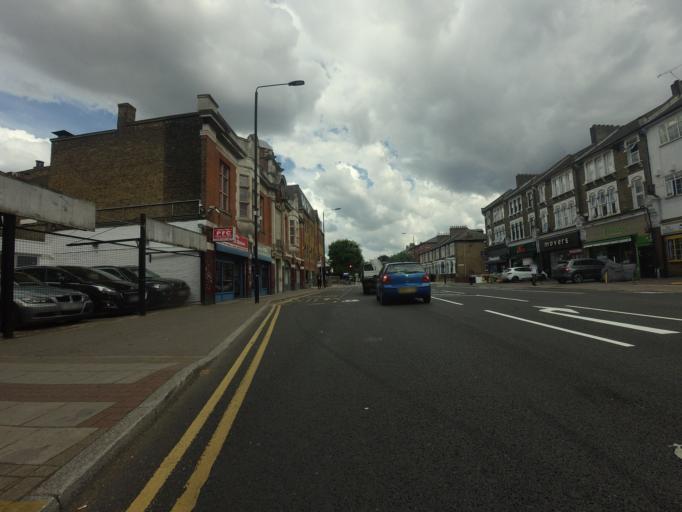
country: GB
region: England
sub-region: Greater London
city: Poplar
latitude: 51.5423
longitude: 0.0059
